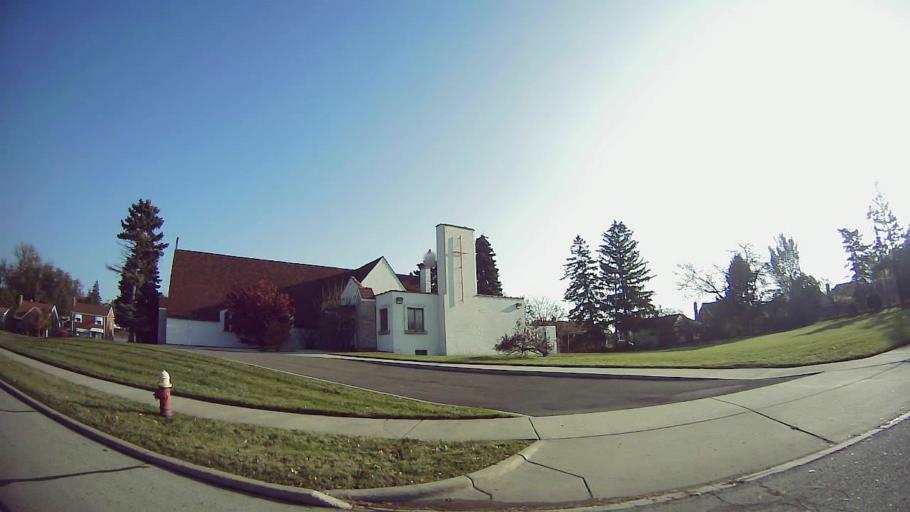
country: US
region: Michigan
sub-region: Wayne County
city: Dearborn
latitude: 42.3519
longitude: -83.1697
